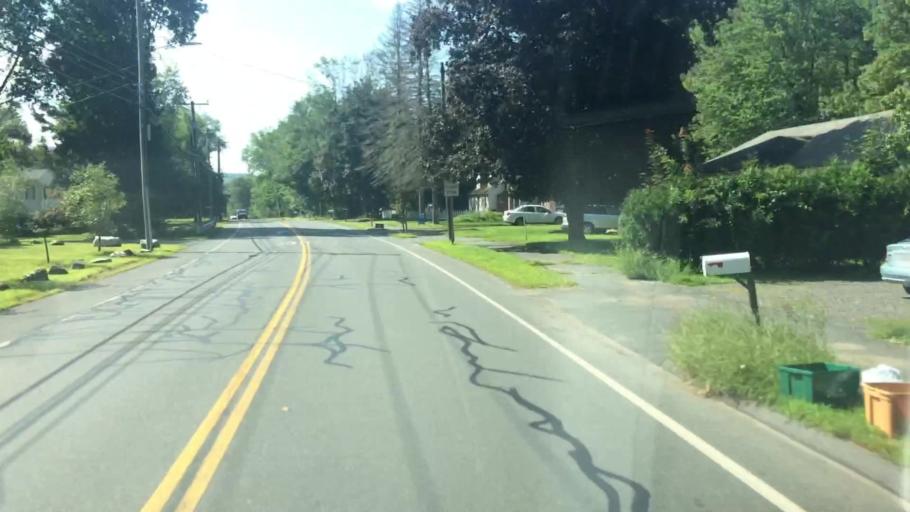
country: US
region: Massachusetts
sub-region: Hampshire County
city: South Amherst
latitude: 42.3468
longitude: -72.5205
